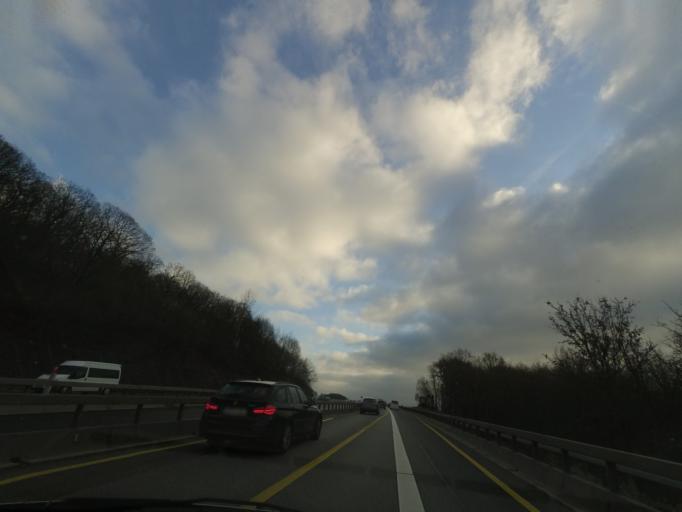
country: DE
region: Hesse
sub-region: Regierungsbezirk Giessen
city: Sinn
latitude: 50.6304
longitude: 8.3322
